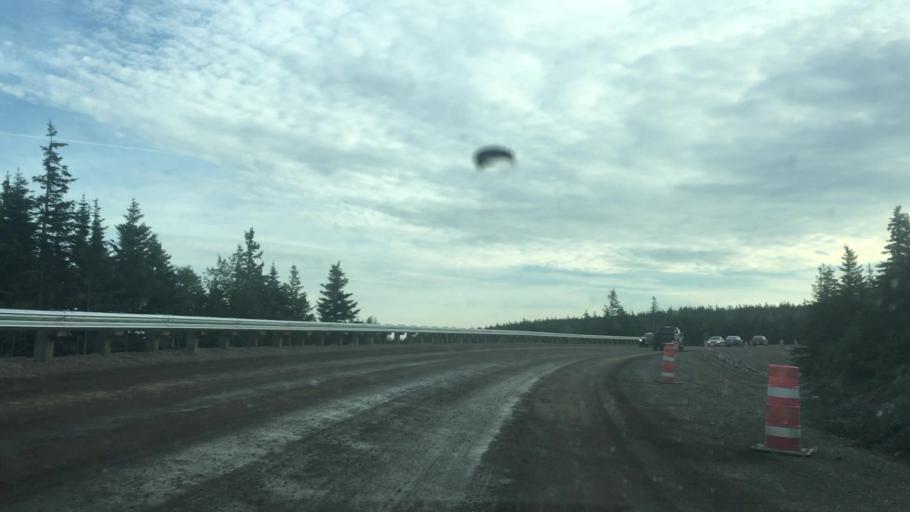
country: CA
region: Nova Scotia
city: Sydney Mines
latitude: 46.8089
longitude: -60.8421
